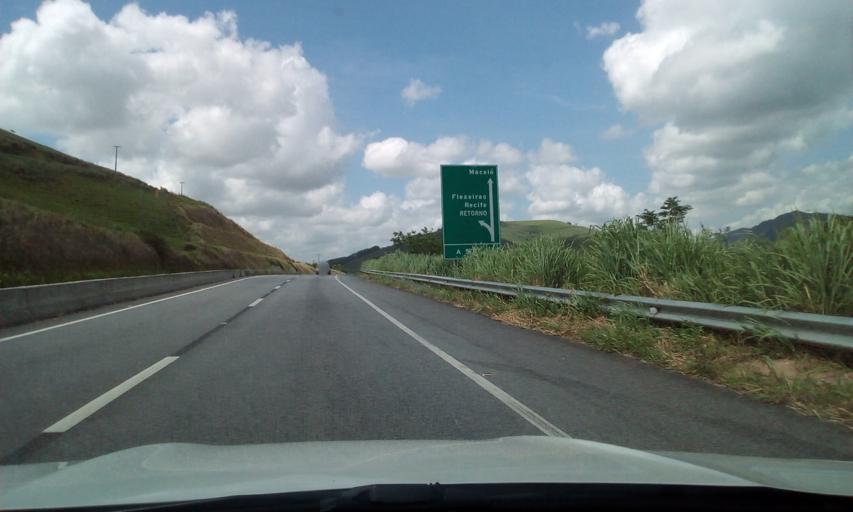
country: BR
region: Alagoas
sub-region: Flexeiras
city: Flexeiras
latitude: -9.2512
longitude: -35.7691
